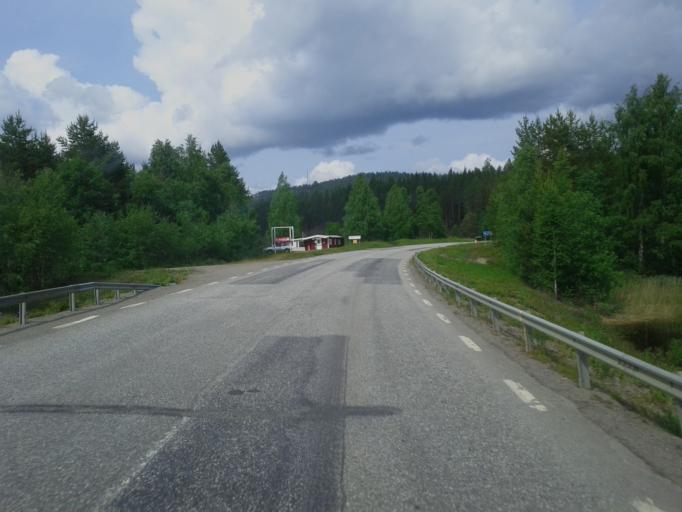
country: SE
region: Vaesterbotten
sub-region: Mala Kommun
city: Mala
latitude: 65.1618
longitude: 18.7816
